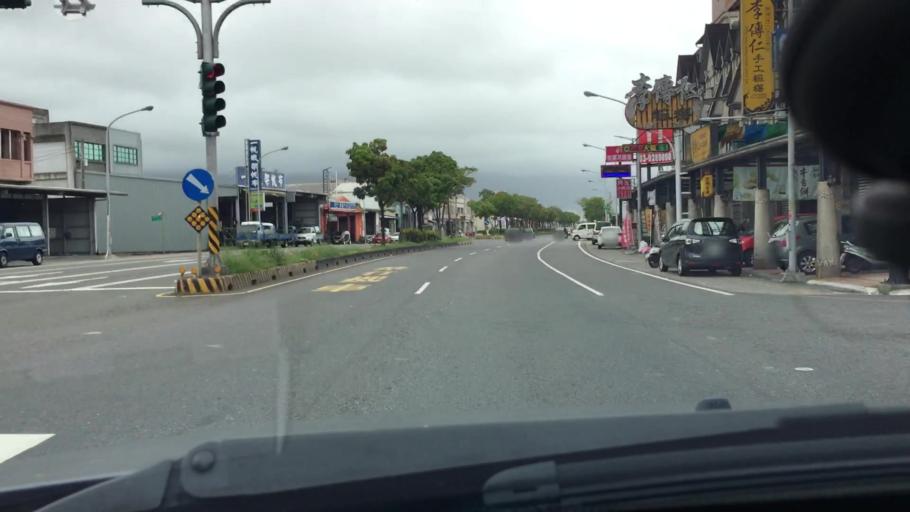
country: TW
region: Taiwan
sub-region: Yilan
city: Yilan
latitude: 24.7897
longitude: 121.7620
